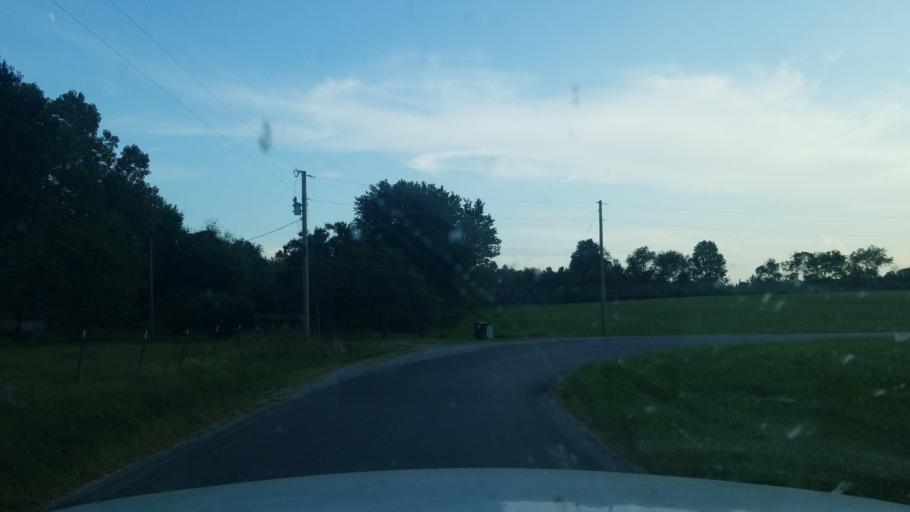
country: US
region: Illinois
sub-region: Saline County
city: Carrier Mills
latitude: 37.7910
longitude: -88.6609
